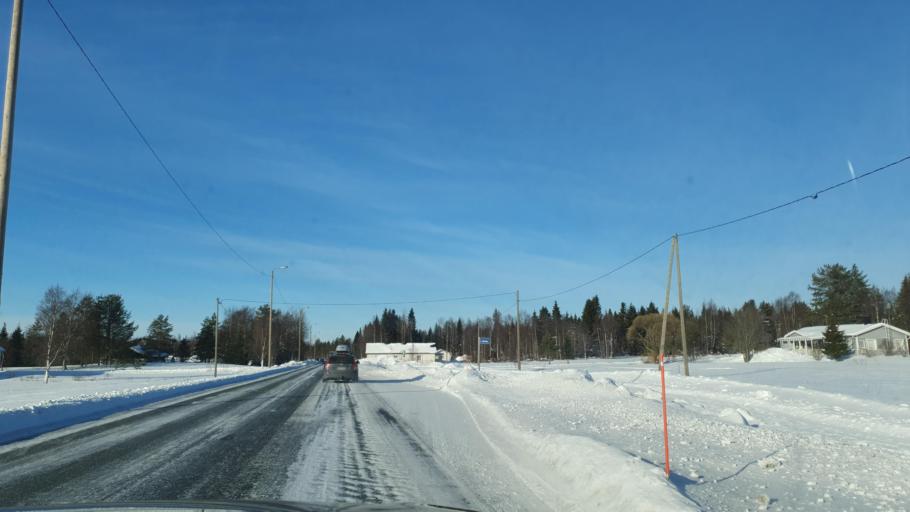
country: FI
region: Lapland
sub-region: Torniolaakso
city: Ylitornio
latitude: 66.2408
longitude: 23.7414
